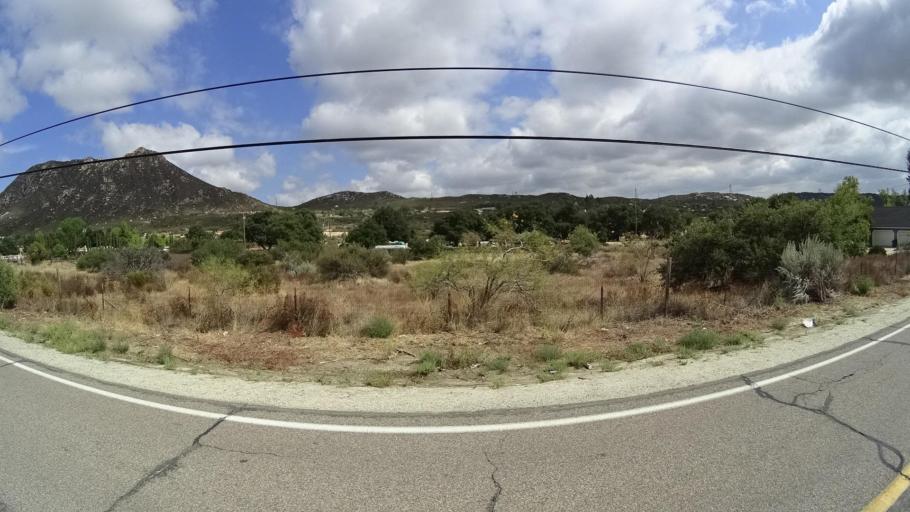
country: US
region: California
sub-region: San Diego County
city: Campo
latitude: 32.6739
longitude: -116.4886
